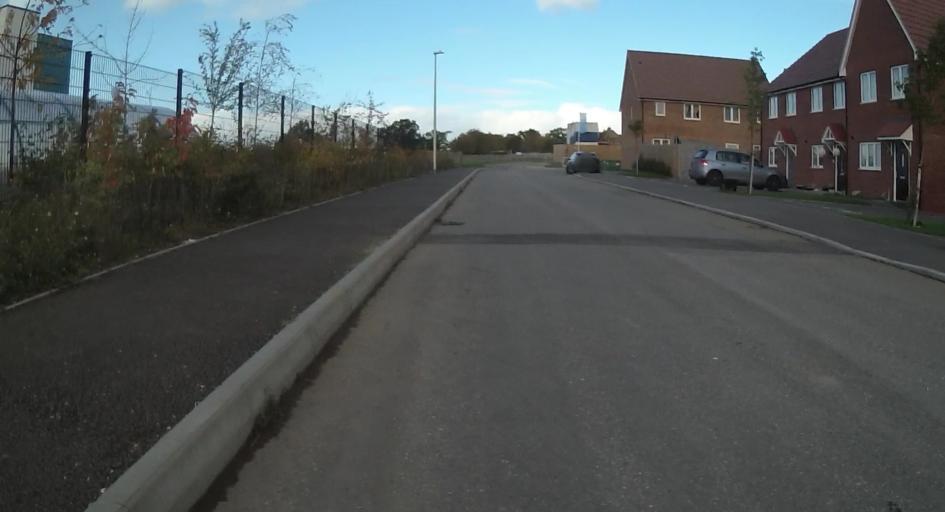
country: GB
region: England
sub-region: Wokingham
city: Shinfield
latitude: 51.4049
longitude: -0.9563
